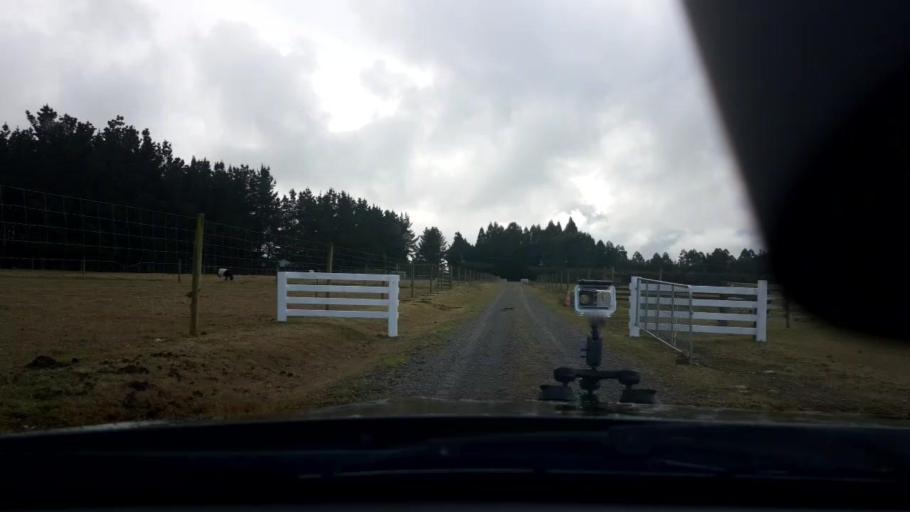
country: NZ
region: Canterbury
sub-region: Waimakariri District
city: Oxford
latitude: -43.4010
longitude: 172.3121
